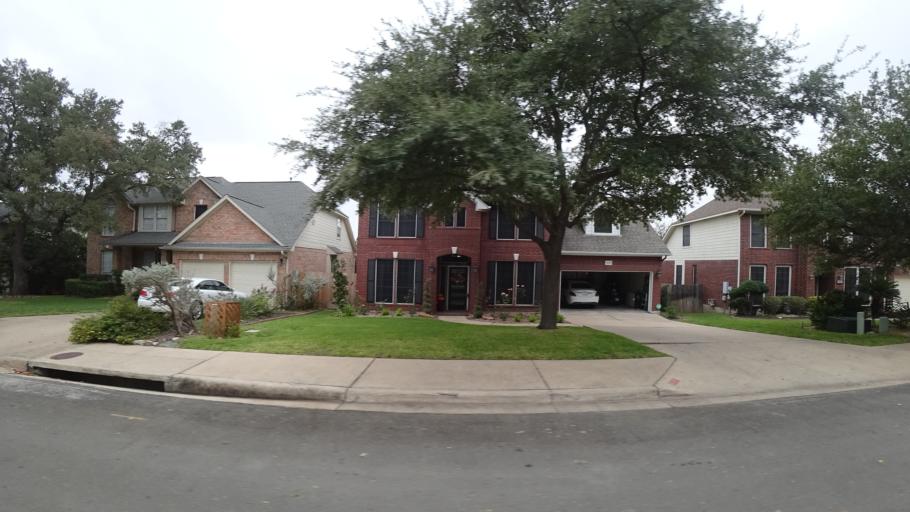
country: US
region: Texas
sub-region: Williamson County
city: Anderson Mill
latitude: 30.4354
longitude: -97.8276
